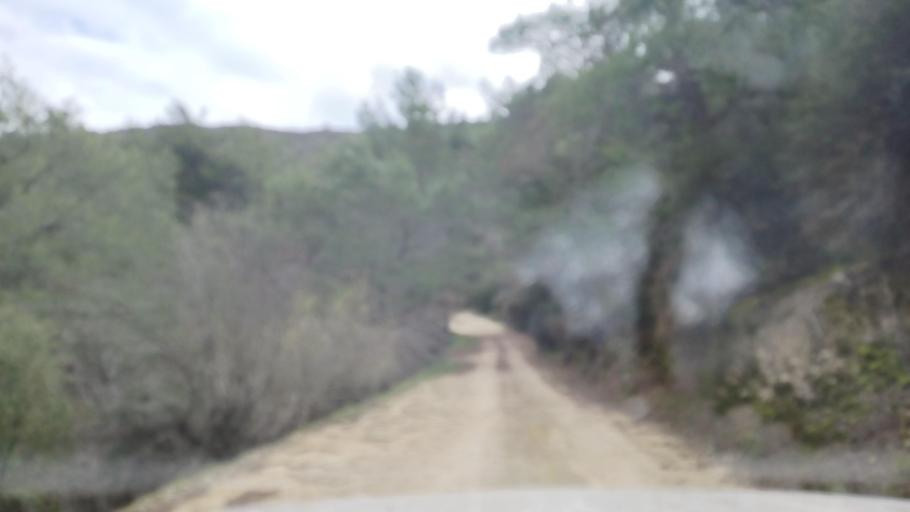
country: CY
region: Limassol
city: Pachna
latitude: 34.7704
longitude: 32.6946
